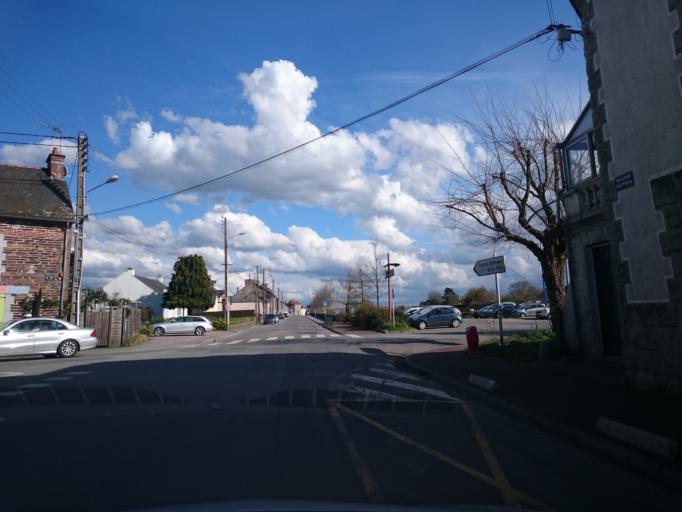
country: FR
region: Brittany
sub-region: Departement d'Ille-et-Vilaine
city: Janze
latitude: 47.9560
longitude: -1.4979
